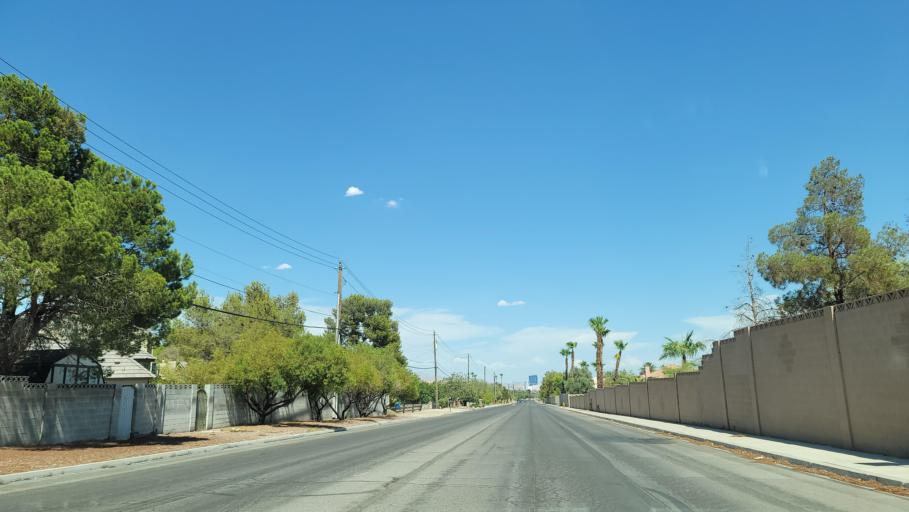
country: US
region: Nevada
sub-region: Clark County
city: Spring Valley
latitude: 36.1366
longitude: -115.2517
